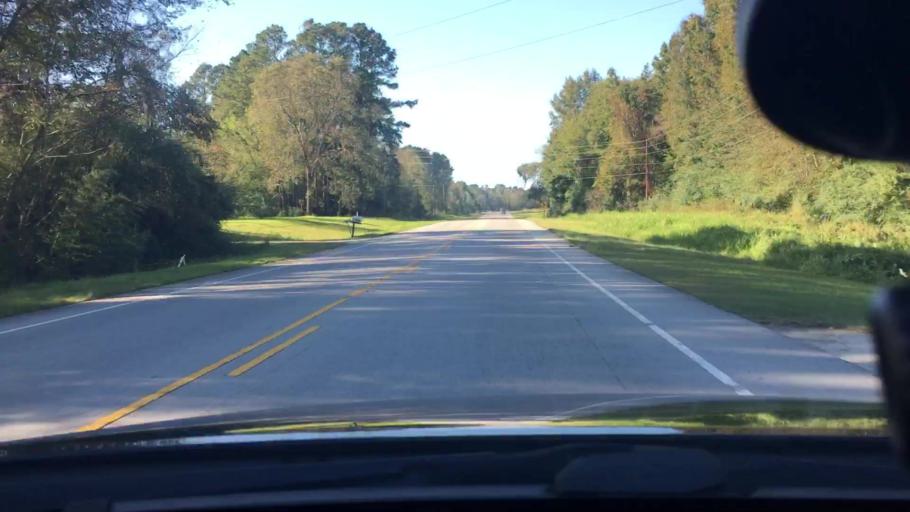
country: US
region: North Carolina
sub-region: Craven County
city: Trent Woods
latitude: 35.1687
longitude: -77.1248
